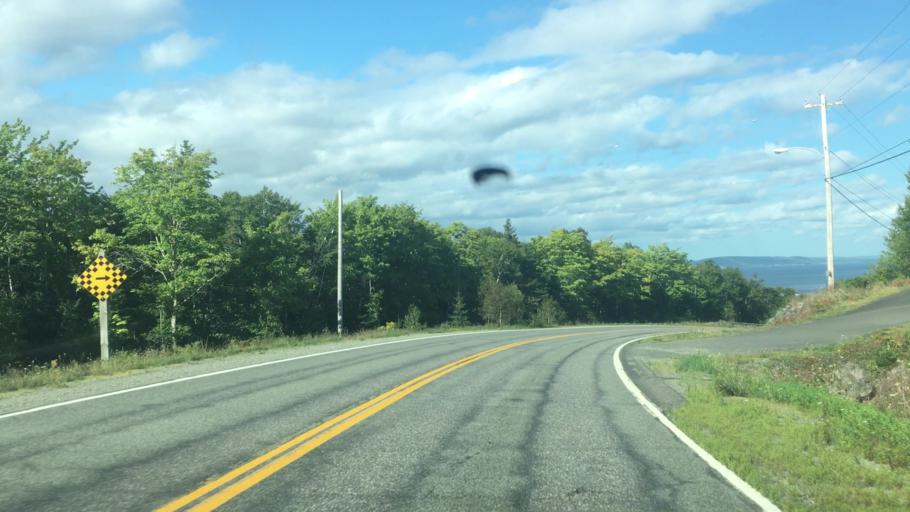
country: CA
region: Nova Scotia
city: Sydney
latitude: 45.8634
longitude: -60.6251
